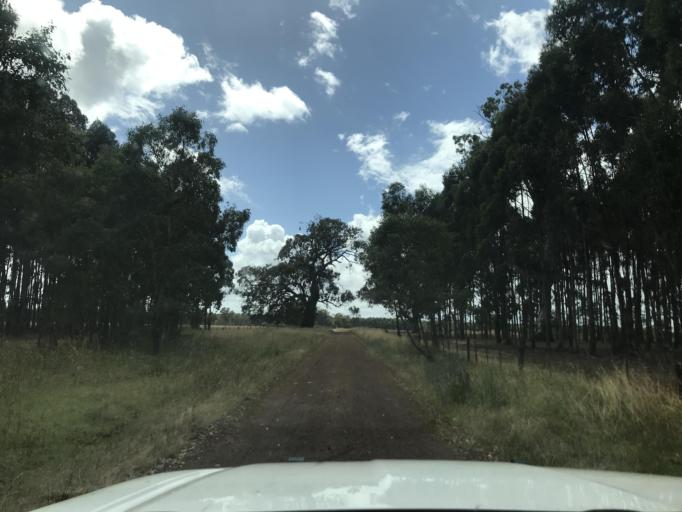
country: AU
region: South Australia
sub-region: Wattle Range
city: Penola
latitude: -37.1909
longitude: 141.3877
